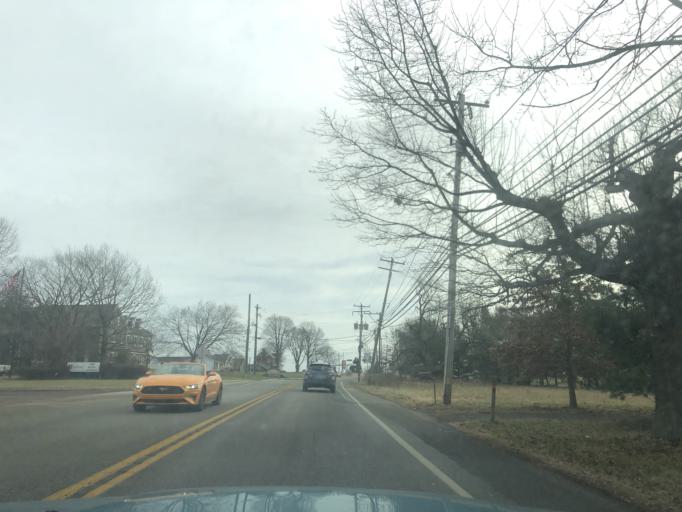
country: US
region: Pennsylvania
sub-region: Montgomery County
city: Harleysville
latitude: 40.2640
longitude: -75.3707
